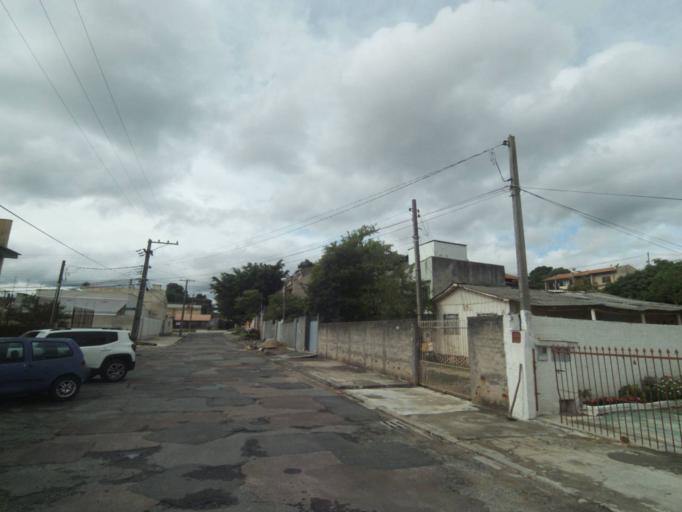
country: BR
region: Parana
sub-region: Curitiba
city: Curitiba
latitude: -25.4424
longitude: -49.3141
